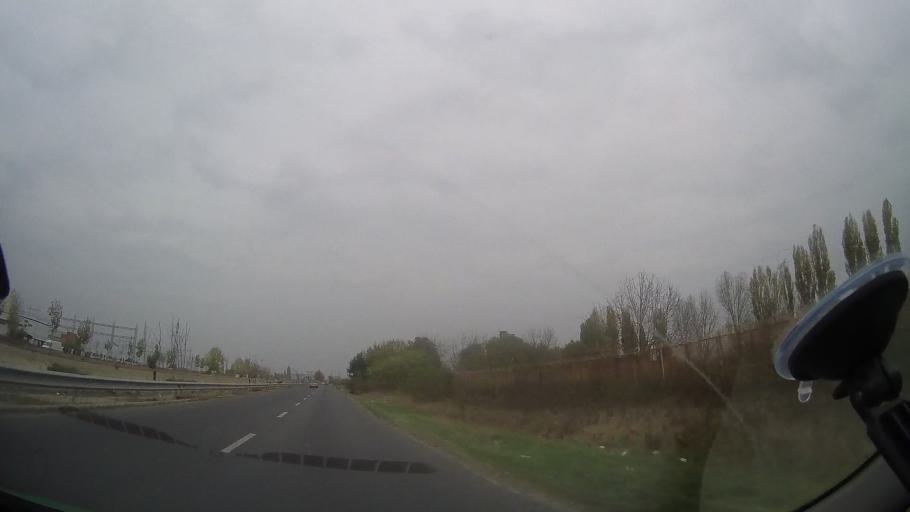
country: RO
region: Ilfov
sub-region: Comuna Popesti-Leordeni
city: Popesti-Leordeni
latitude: 44.3963
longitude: 26.1702
